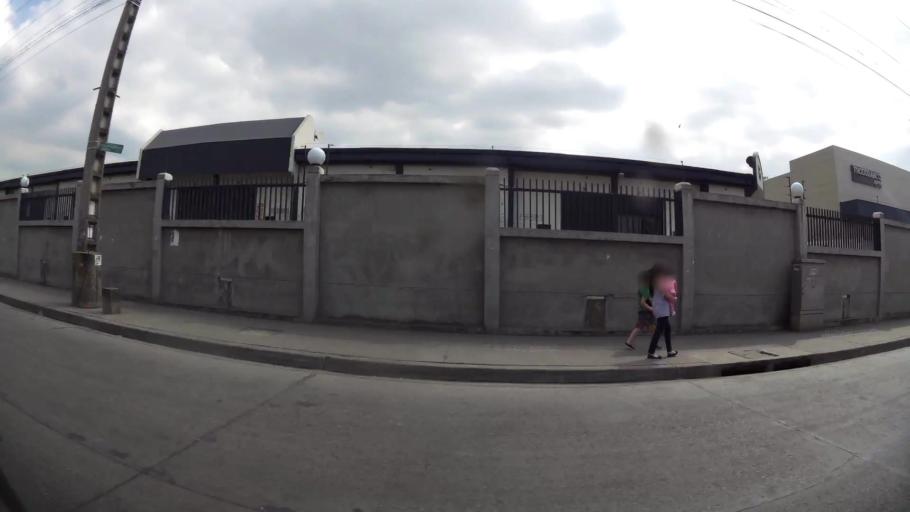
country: EC
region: Guayas
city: Santa Lucia
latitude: -2.0963
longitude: -79.9364
